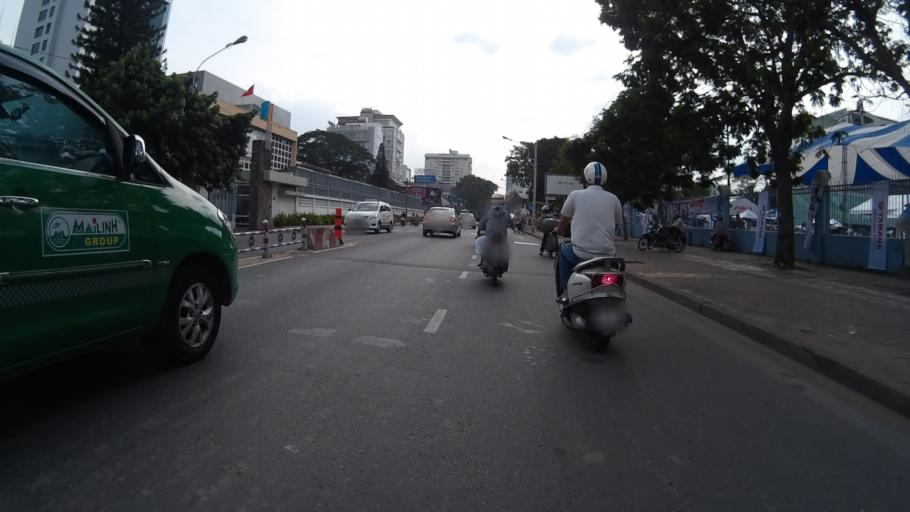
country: VN
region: Ho Chi Minh City
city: Quan Mot
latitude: 10.7875
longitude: 106.7024
